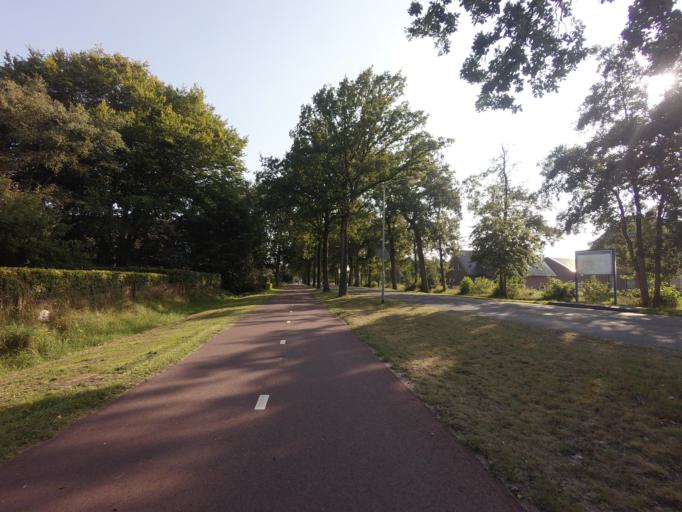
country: NL
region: Groningen
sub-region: Gemeente Groningen
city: Groningen
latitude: 53.1546
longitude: 6.4934
